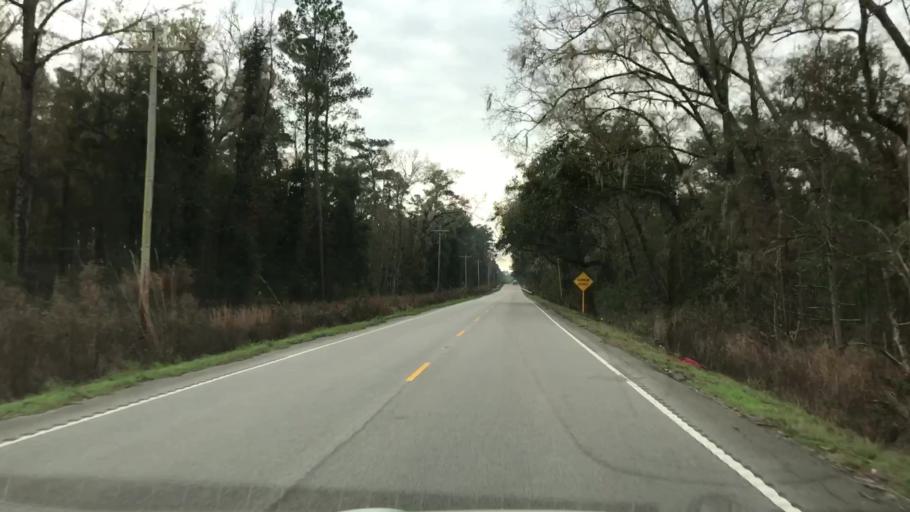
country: US
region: South Carolina
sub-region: Jasper County
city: Ridgeland
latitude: 32.5105
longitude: -80.8883
